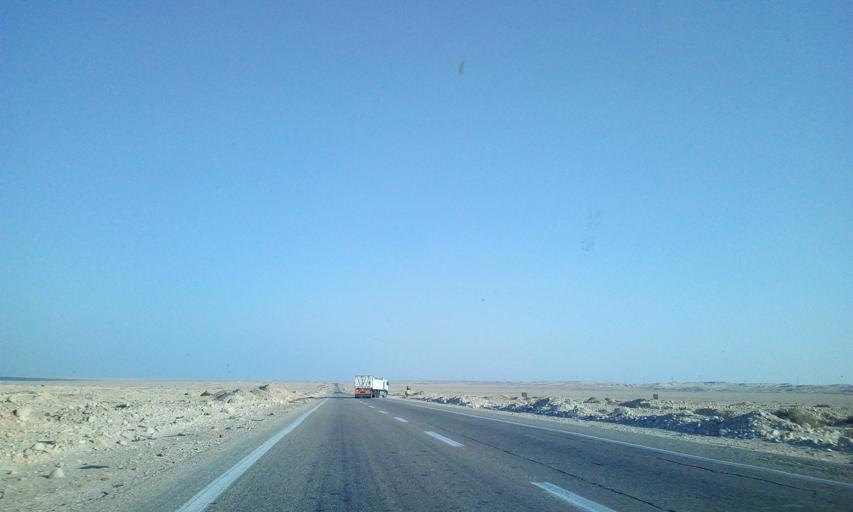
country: EG
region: As Suways
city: Ain Sukhna
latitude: 28.8269
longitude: 32.7169
